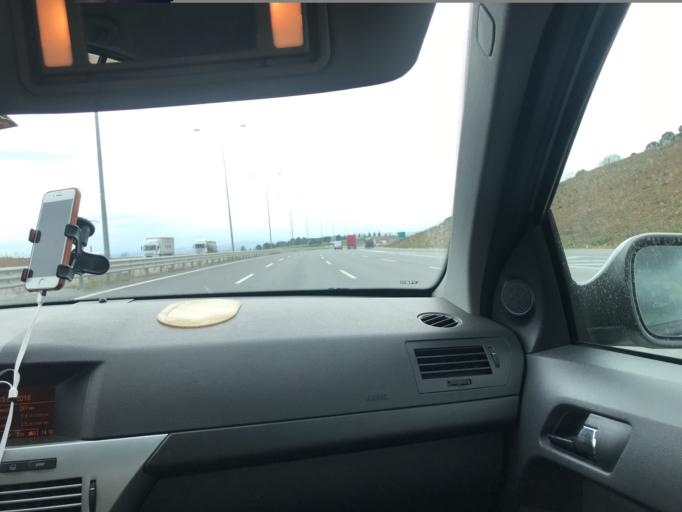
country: TR
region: Istanbul
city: Sultanbeyli
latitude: 40.9919
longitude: 29.3252
